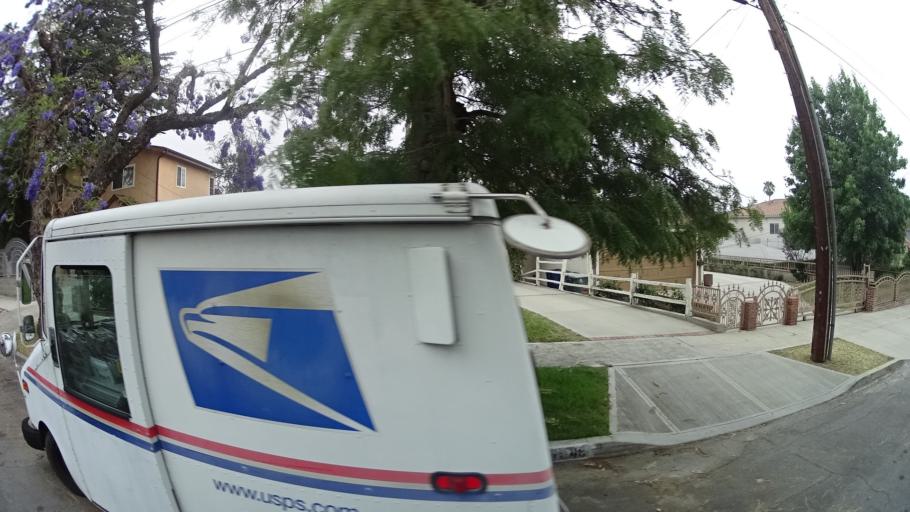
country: US
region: California
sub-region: Los Angeles County
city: Burbank
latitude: 34.1878
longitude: -118.2927
